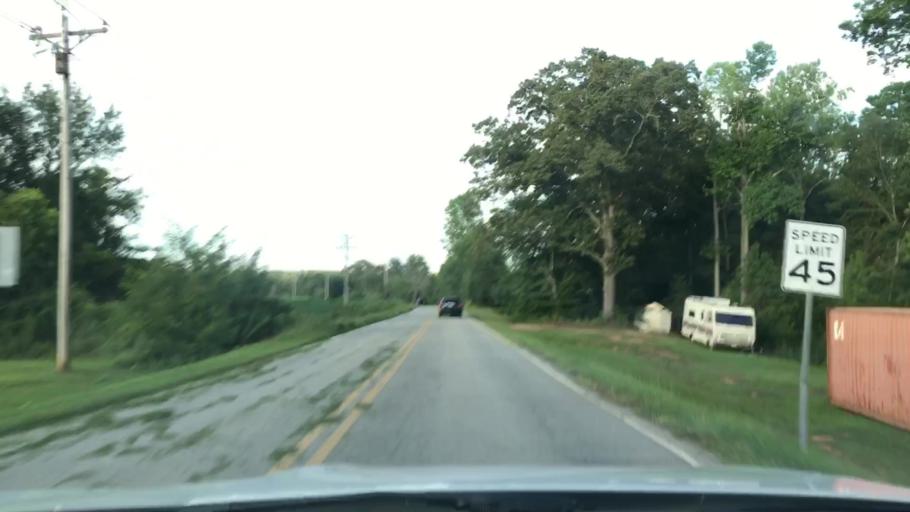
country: US
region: South Carolina
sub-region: Spartanburg County
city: Woodruff
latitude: 34.7481
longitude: -81.9367
